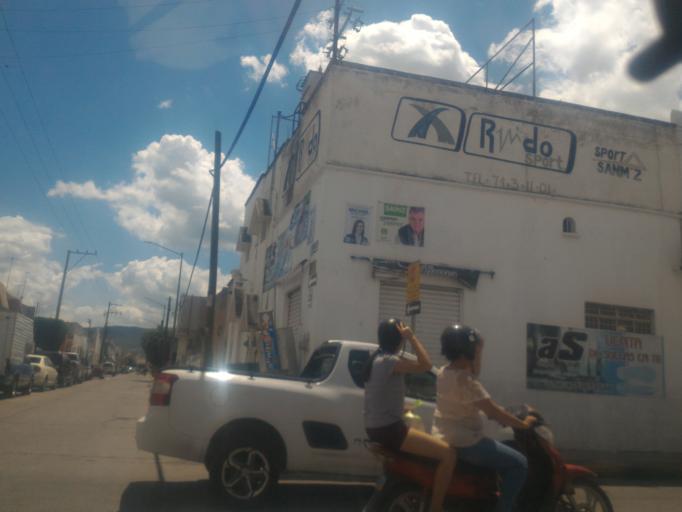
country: MX
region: Guanajuato
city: San Francisco del Rincon
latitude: 21.0189
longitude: -101.8527
